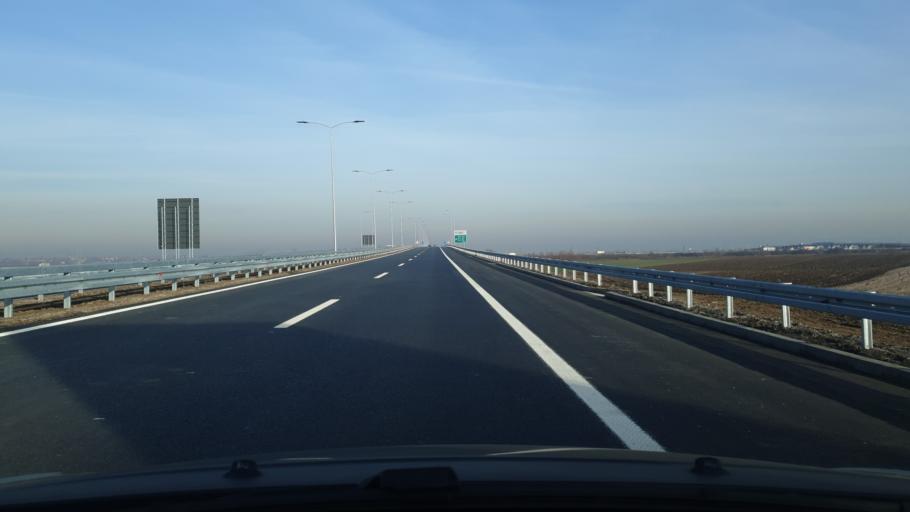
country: RS
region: Central Serbia
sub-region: Belgrade
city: Surcin
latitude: 44.7699
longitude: 20.2644
